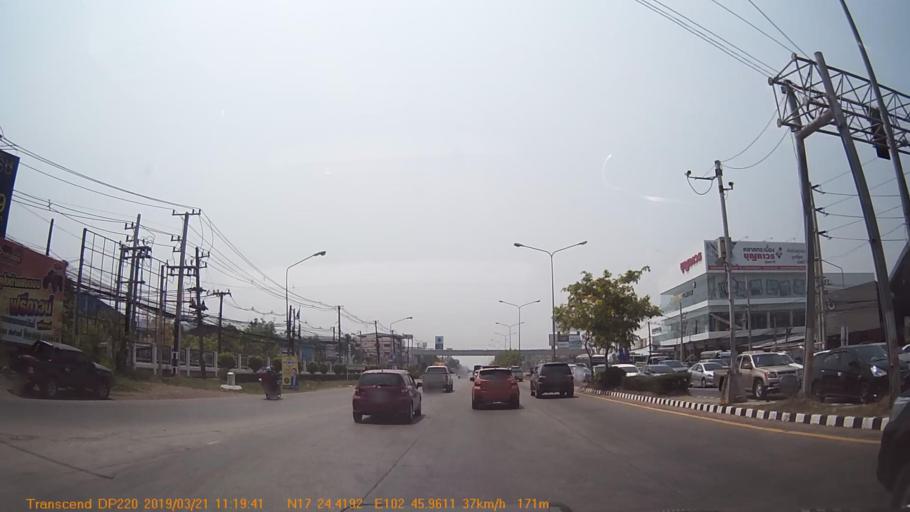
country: TH
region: Changwat Udon Thani
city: Udon Thani
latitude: 17.4069
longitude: 102.7660
